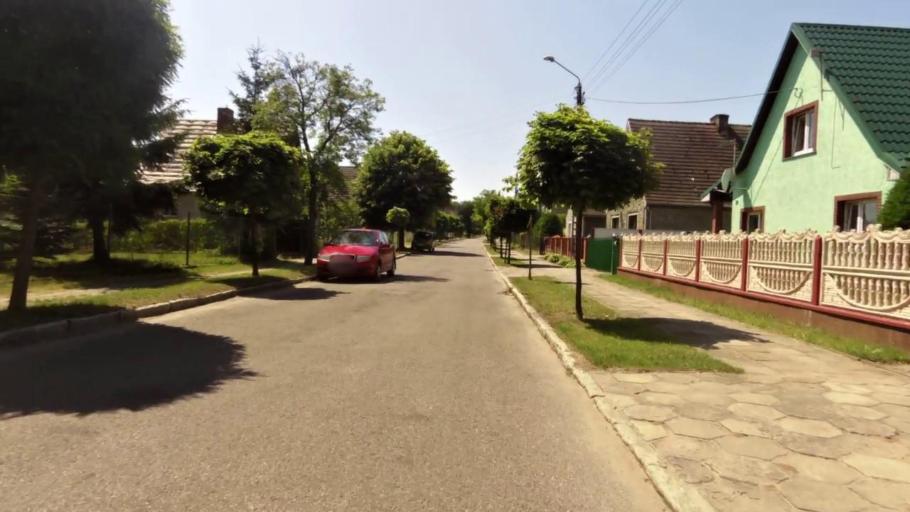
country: PL
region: West Pomeranian Voivodeship
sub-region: Powiat swidwinski
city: Polczyn-Zdroj
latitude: 53.7733
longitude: 16.1058
